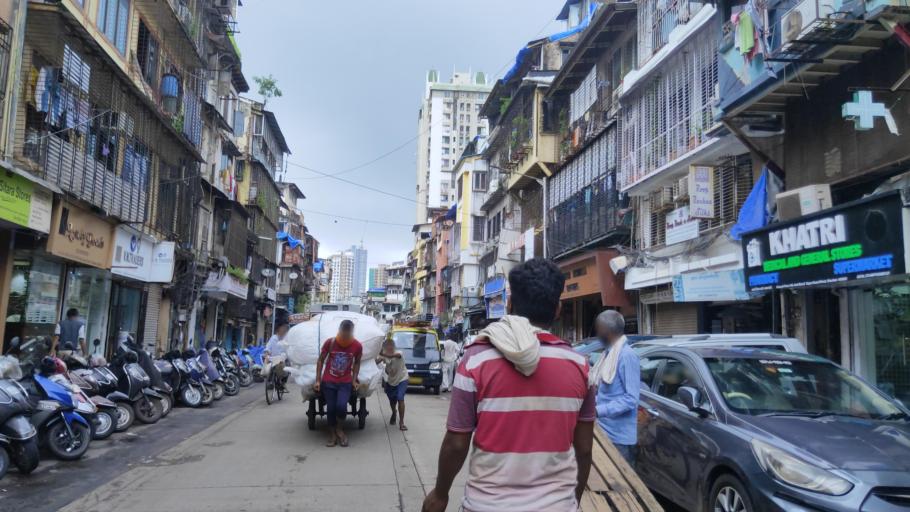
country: IN
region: Maharashtra
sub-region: Mumbai Suburban
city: Mumbai
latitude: 18.9547
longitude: 72.8305
